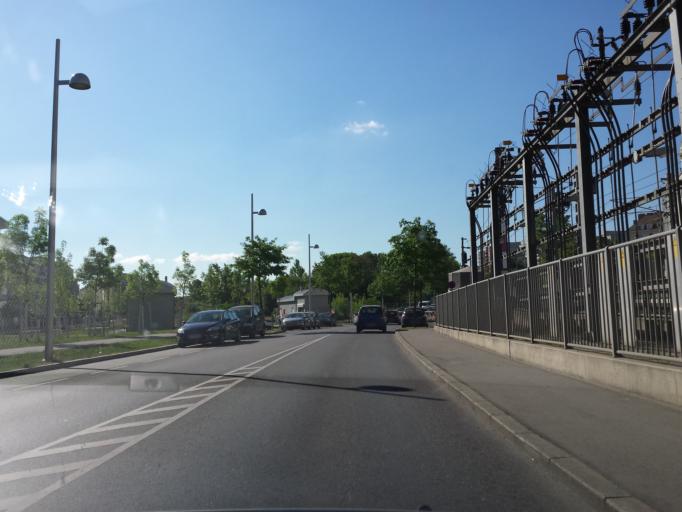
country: AT
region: Vienna
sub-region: Wien Stadt
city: Vienna
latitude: 48.1921
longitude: 16.3910
